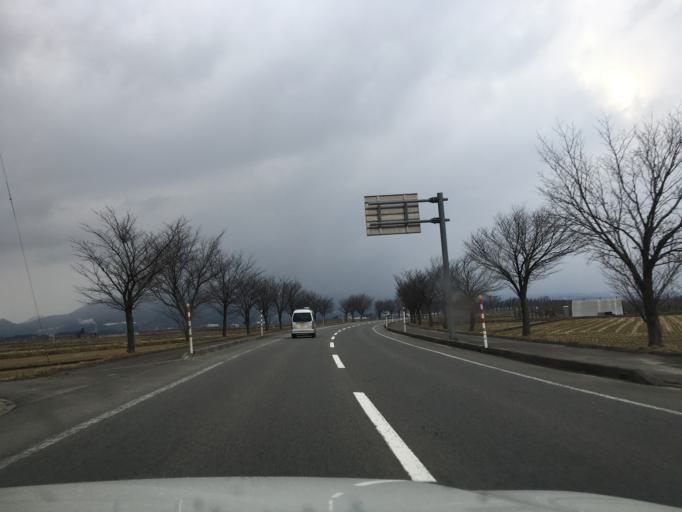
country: JP
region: Aomori
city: Kuroishi
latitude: 40.5700
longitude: 140.5664
